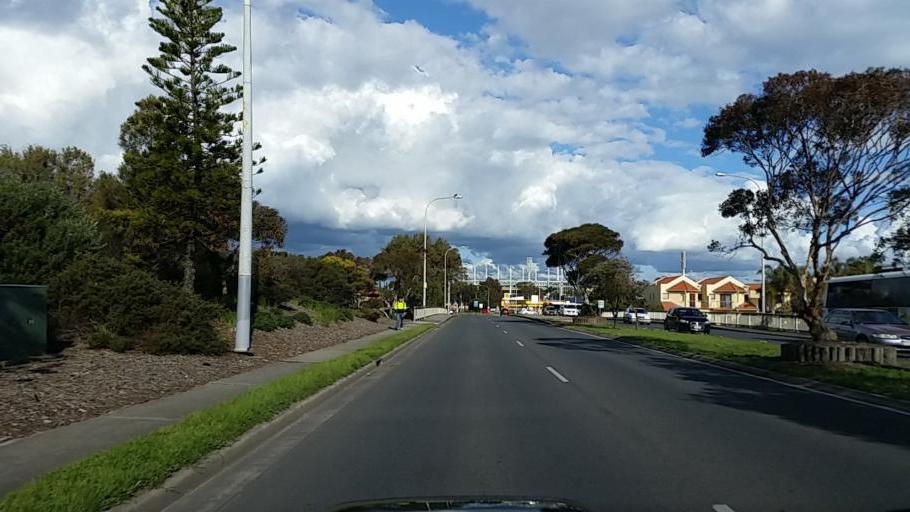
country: AU
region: South Australia
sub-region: Charles Sturt
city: West Lakes Shore
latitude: -34.8750
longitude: 138.4909
